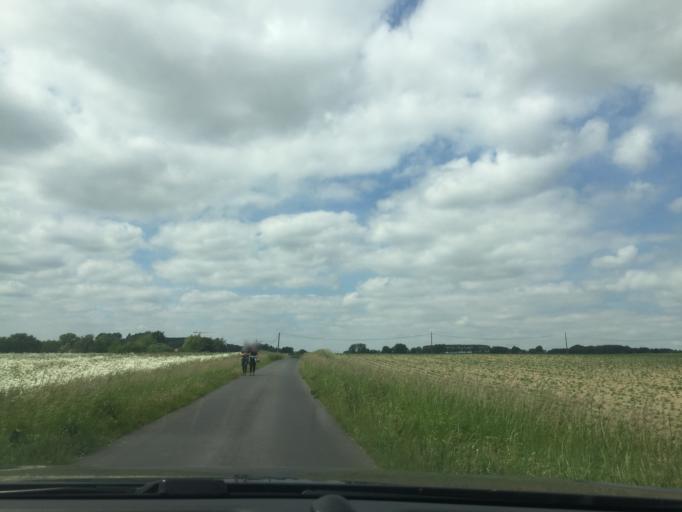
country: BE
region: Flanders
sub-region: Provincie West-Vlaanderen
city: Zwevegem
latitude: 50.7631
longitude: 3.3473
